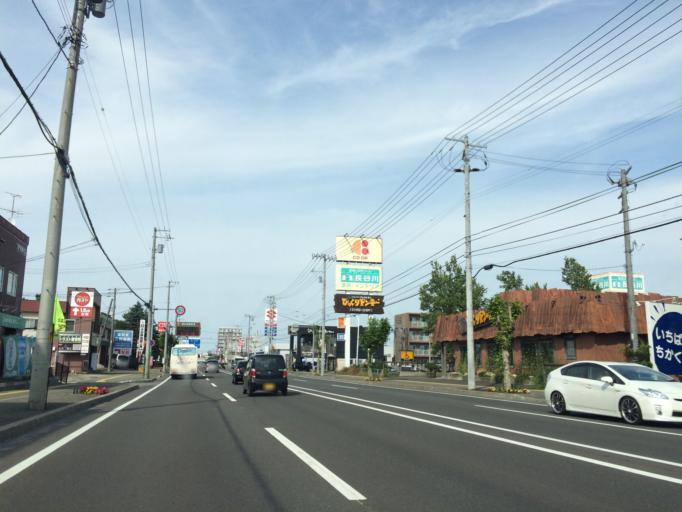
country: JP
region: Hokkaido
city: Ebetsu
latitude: 43.0900
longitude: 141.5192
